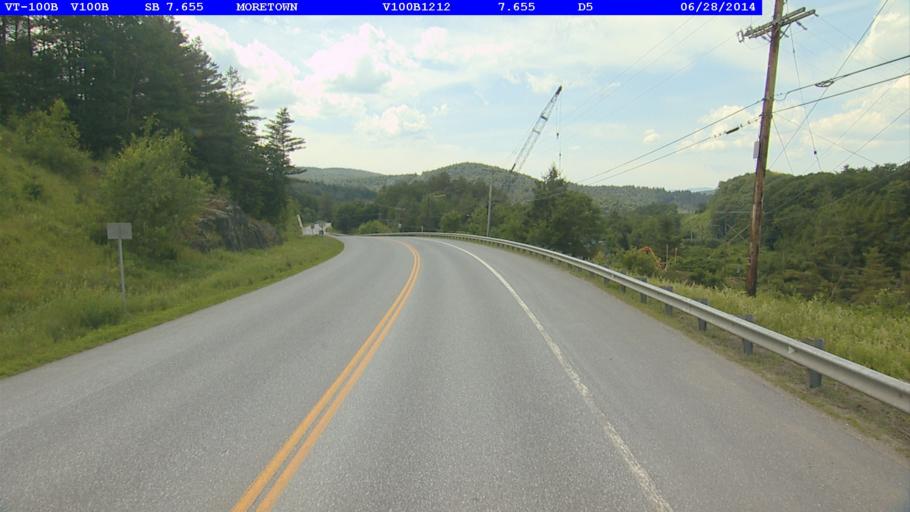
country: US
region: Vermont
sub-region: Washington County
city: Waterbury
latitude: 44.2914
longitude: -72.6824
